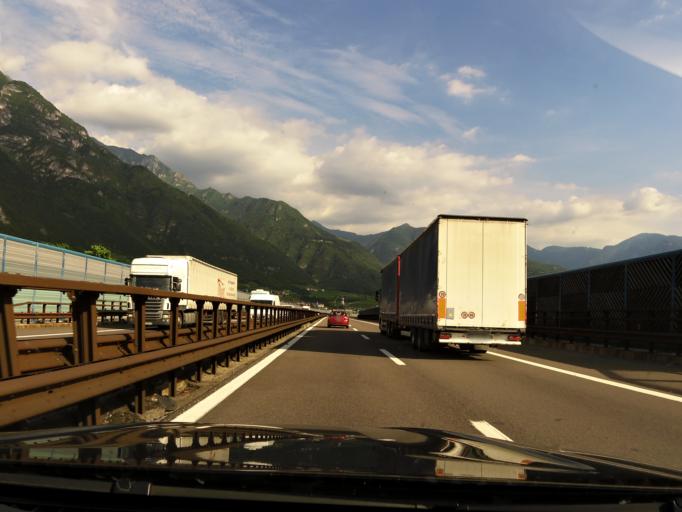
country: IT
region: Trentino-Alto Adige
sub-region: Provincia di Trento
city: Marco
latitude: 45.8092
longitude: 11.0128
